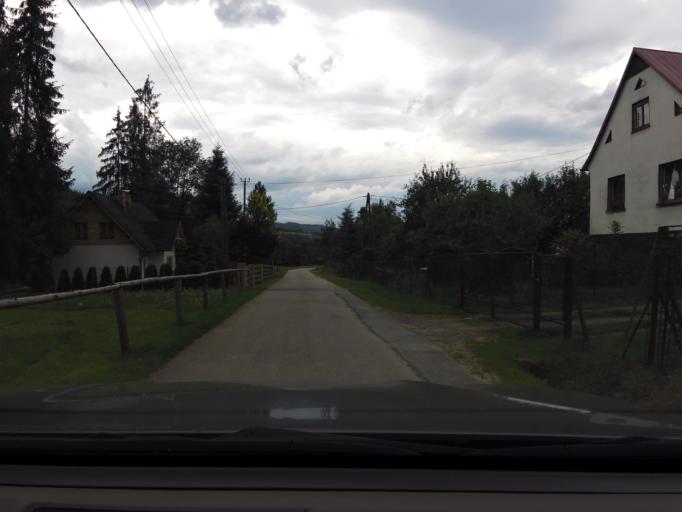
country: PL
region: Silesian Voivodeship
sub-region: Powiat zywiecki
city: Ujsoly
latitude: 49.5082
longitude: 19.1450
